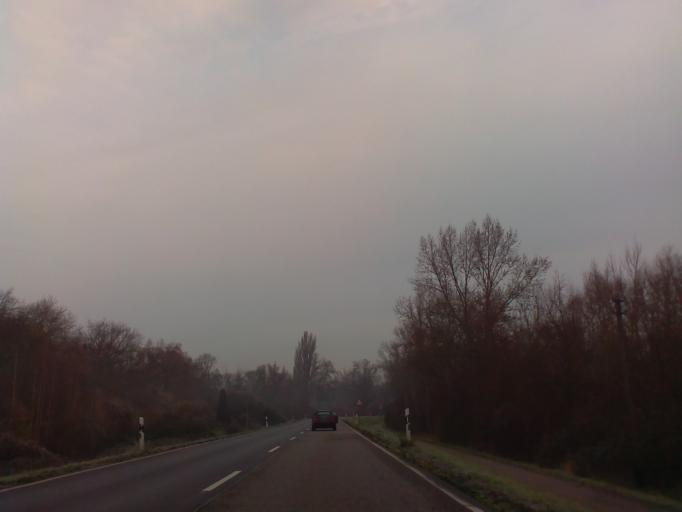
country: DE
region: Rheinland-Pfalz
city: Neuhofen
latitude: 49.4378
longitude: 8.4533
